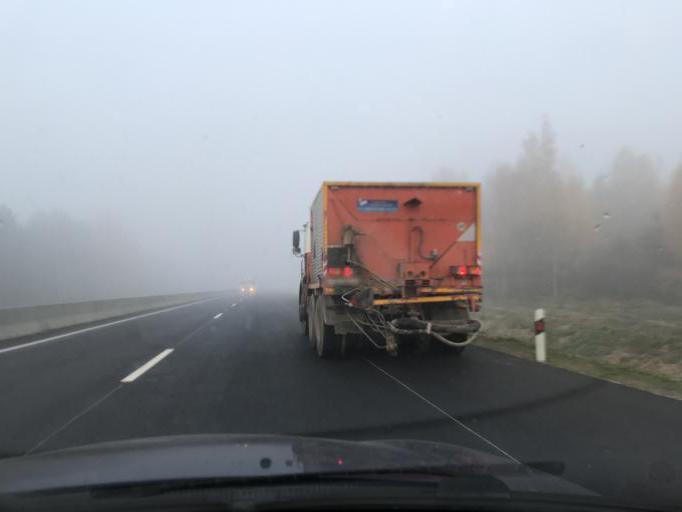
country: BY
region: Minsk
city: Valozhyn
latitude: 54.0402
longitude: 26.5912
